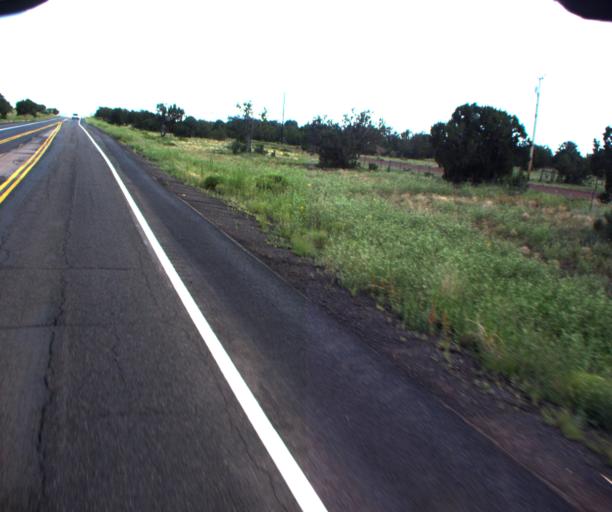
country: US
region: Arizona
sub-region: Coconino County
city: Williams
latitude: 35.3517
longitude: -112.1670
